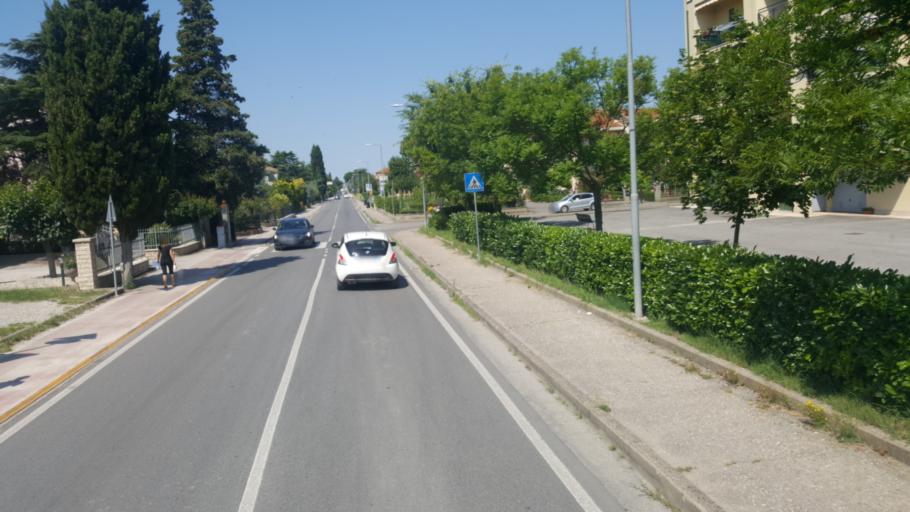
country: IT
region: Umbria
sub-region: Provincia di Perugia
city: Castiglione del Lago
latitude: 43.1258
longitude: 12.0415
